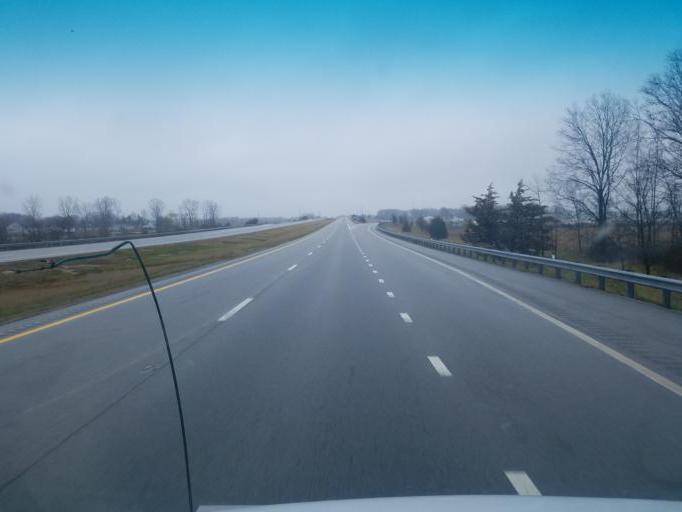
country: US
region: Ohio
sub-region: Wood County
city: Bowling Green
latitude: 41.3490
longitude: -83.6564
